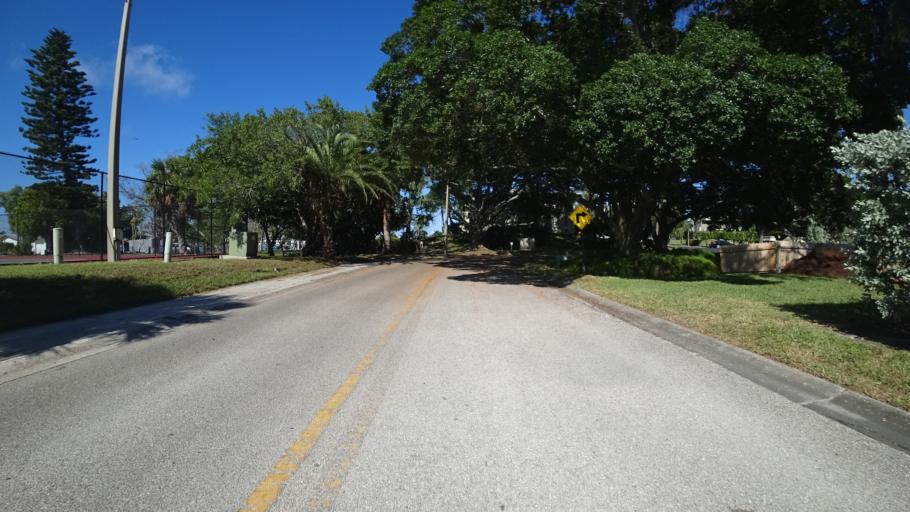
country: US
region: Florida
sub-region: Manatee County
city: Holmes Beach
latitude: 27.5129
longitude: -82.7136
